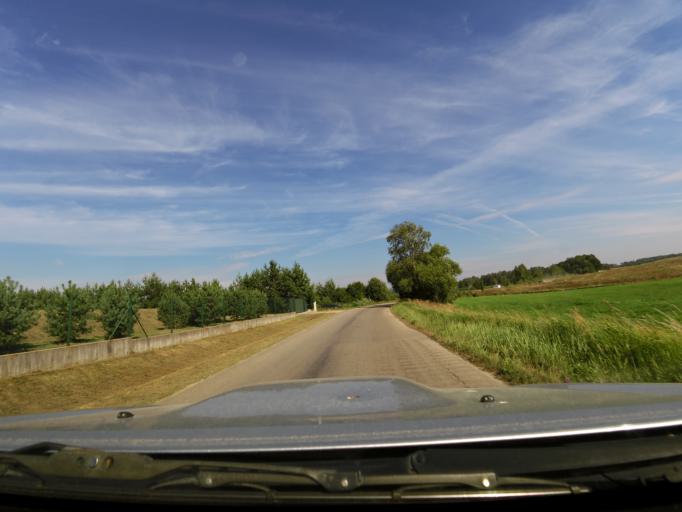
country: LT
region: Vilnius County
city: Pasilaiciai
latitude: 54.8339
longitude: 25.1607
